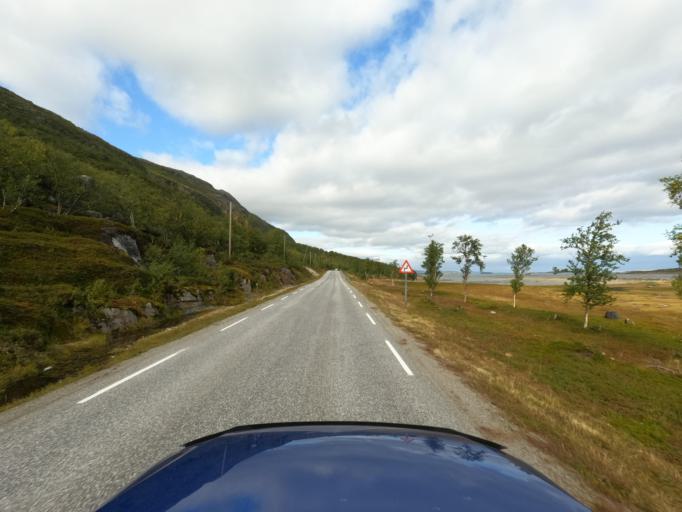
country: NO
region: Finnmark Fylke
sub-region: Porsanger
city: Lakselv
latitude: 70.1146
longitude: 24.9193
